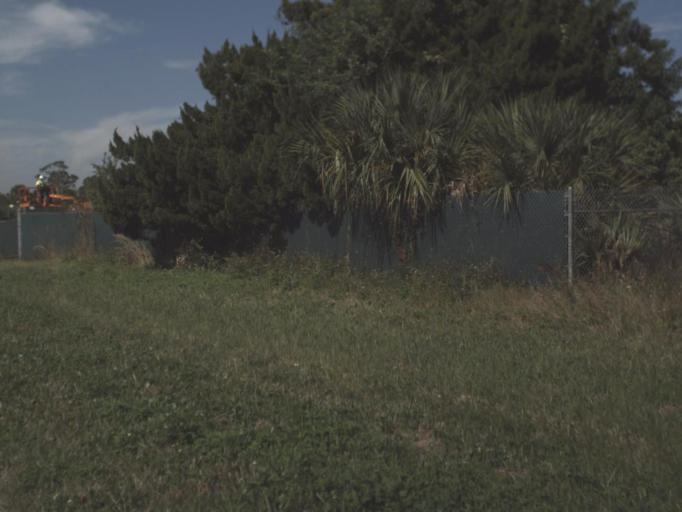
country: US
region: Florida
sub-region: Brevard County
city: Merritt Island
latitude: 28.6436
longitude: -80.7000
